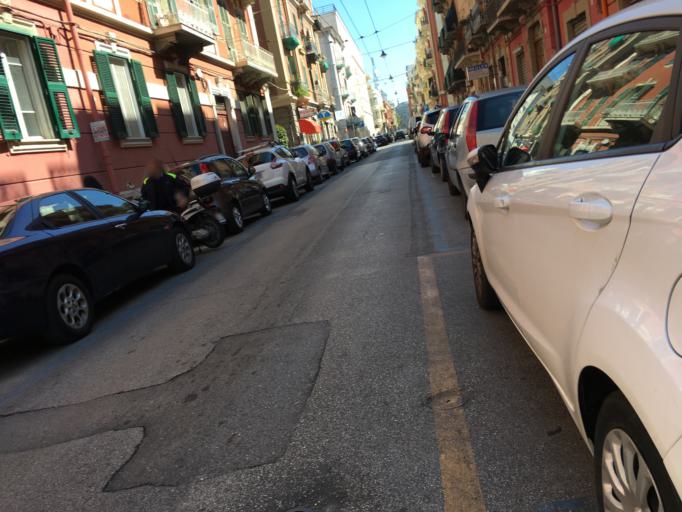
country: IT
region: Apulia
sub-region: Provincia di Bari
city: Bari
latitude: 41.1210
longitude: 16.8809
